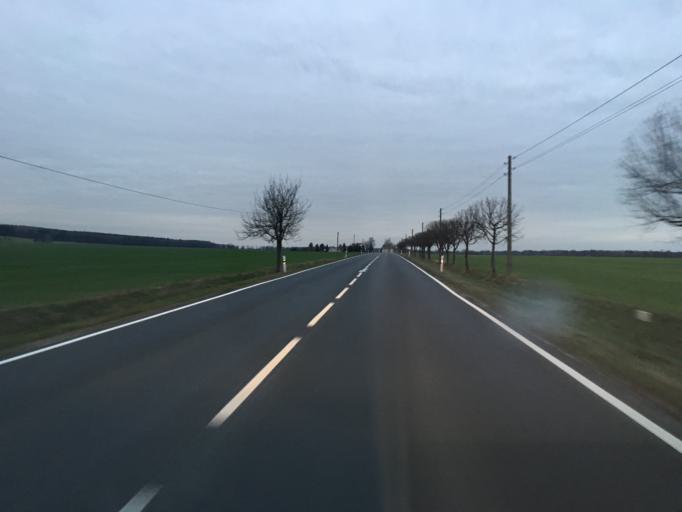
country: DE
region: Saxony
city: Oschatz
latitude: 51.3159
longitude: 13.0757
